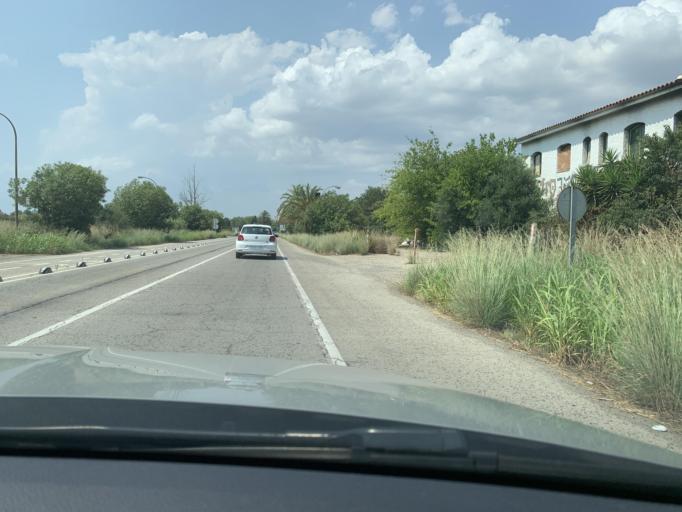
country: ES
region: Catalonia
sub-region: Provincia de Tarragona
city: Torredembarra
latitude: 41.1410
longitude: 1.3918
